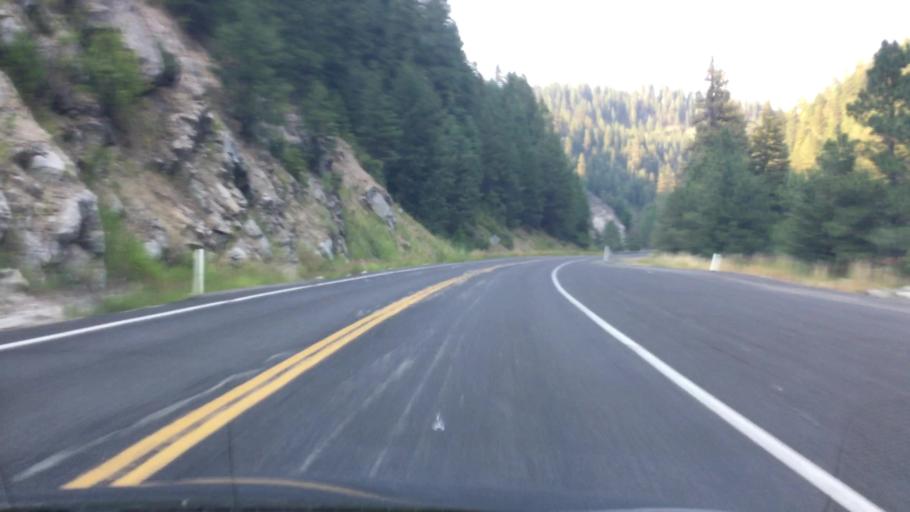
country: US
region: Idaho
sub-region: Valley County
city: Cascade
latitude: 44.2573
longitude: -116.0822
